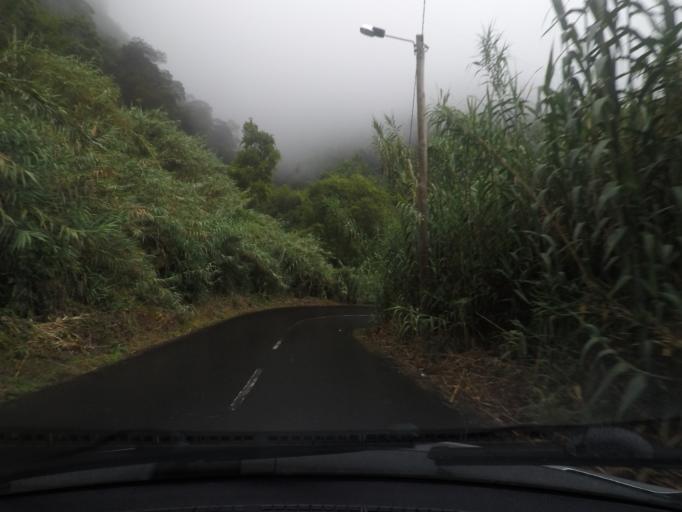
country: PT
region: Madeira
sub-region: Santana
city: Santana
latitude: 32.7754
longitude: -16.8737
